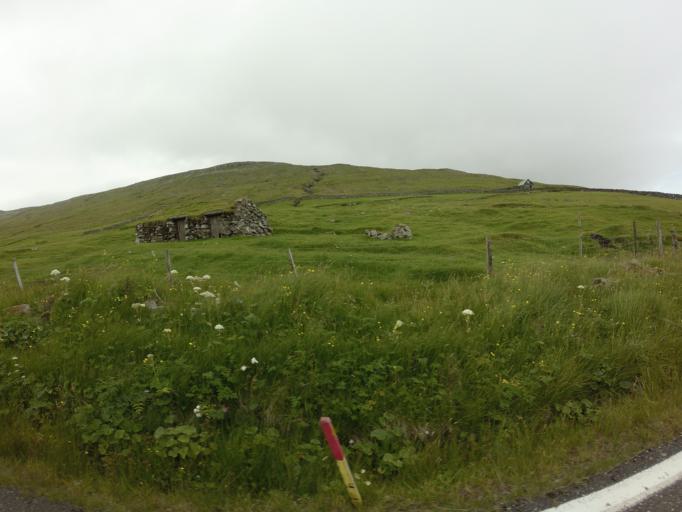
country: FO
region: Sandoy
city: Sandur
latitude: 61.8163
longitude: -6.7079
